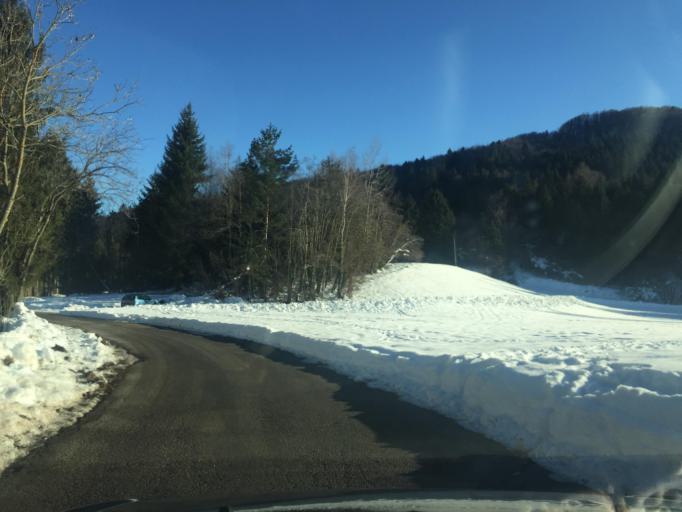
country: IT
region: Friuli Venezia Giulia
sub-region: Provincia di Udine
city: Chiaulis
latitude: 46.4253
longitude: 12.9796
